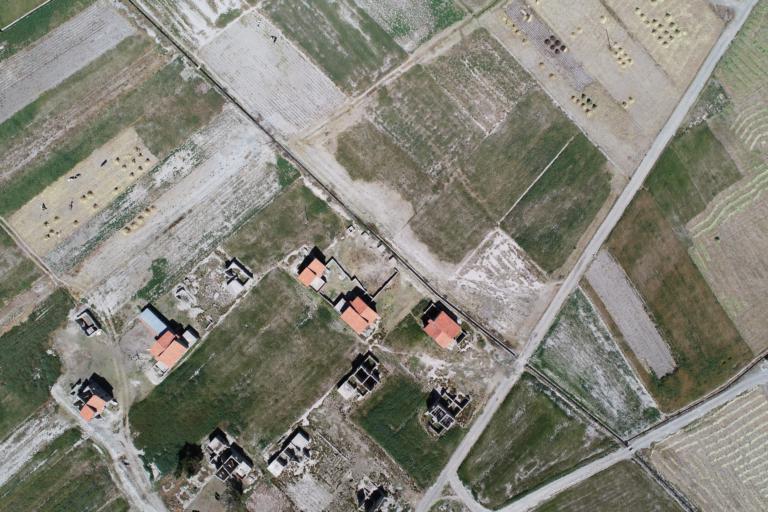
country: BO
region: La Paz
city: Achacachi
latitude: -16.0182
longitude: -68.7176
